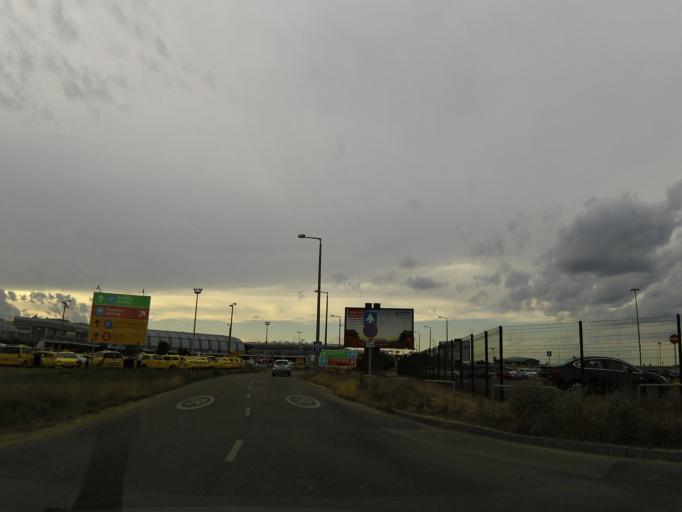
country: HU
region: Pest
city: Vecses
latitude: 47.4295
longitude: 19.2635
